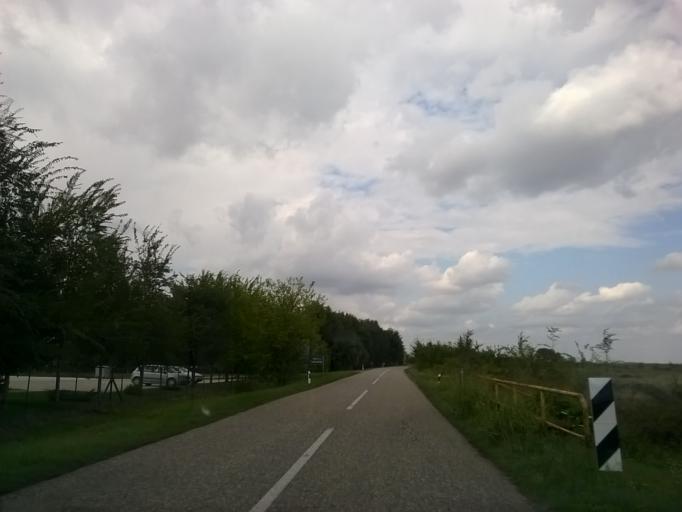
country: RS
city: Barice
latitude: 45.1887
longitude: 21.0866
